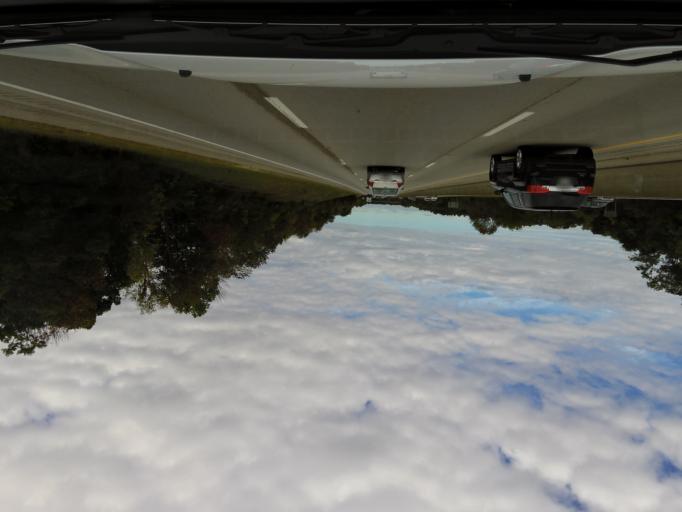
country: US
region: Kentucky
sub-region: Boone County
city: Walton
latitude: 38.8330
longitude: -84.6054
